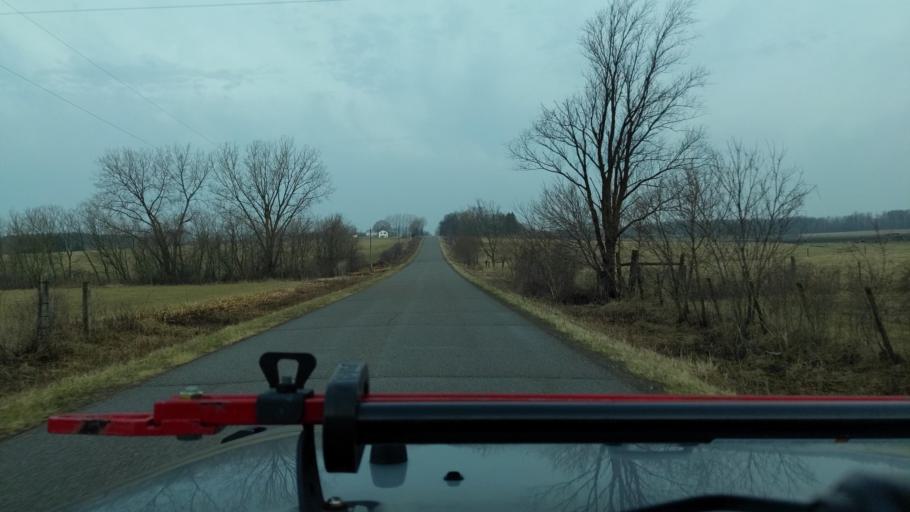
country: US
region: Wisconsin
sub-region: Saint Croix County
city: Baldwin
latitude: 44.9345
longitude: -92.4050
